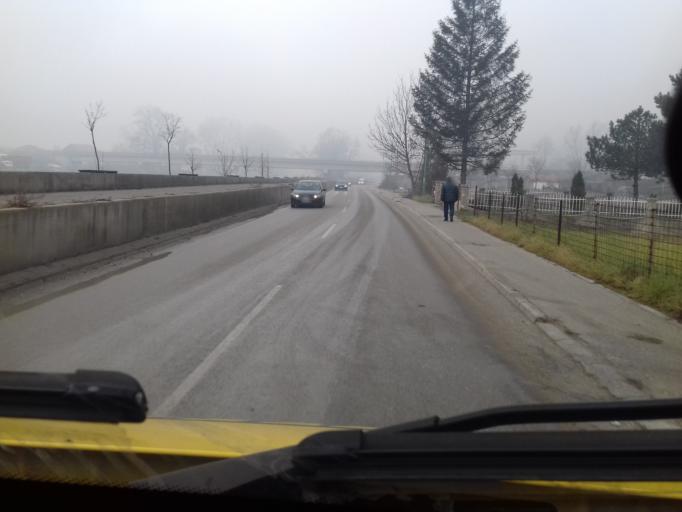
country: BA
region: Federation of Bosnia and Herzegovina
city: Kakanj
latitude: 44.1263
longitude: 18.1076
